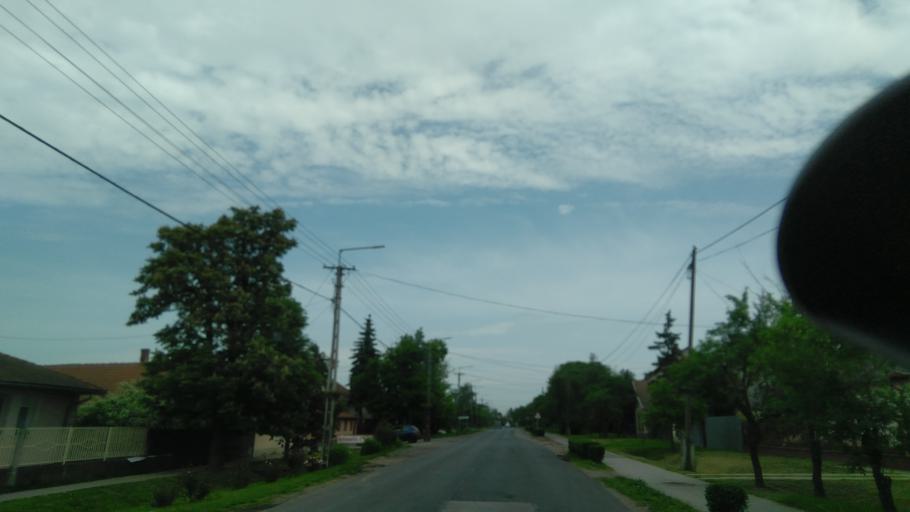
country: HU
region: Bekes
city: Fuzesgyarmat
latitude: 47.0986
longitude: 21.2075
